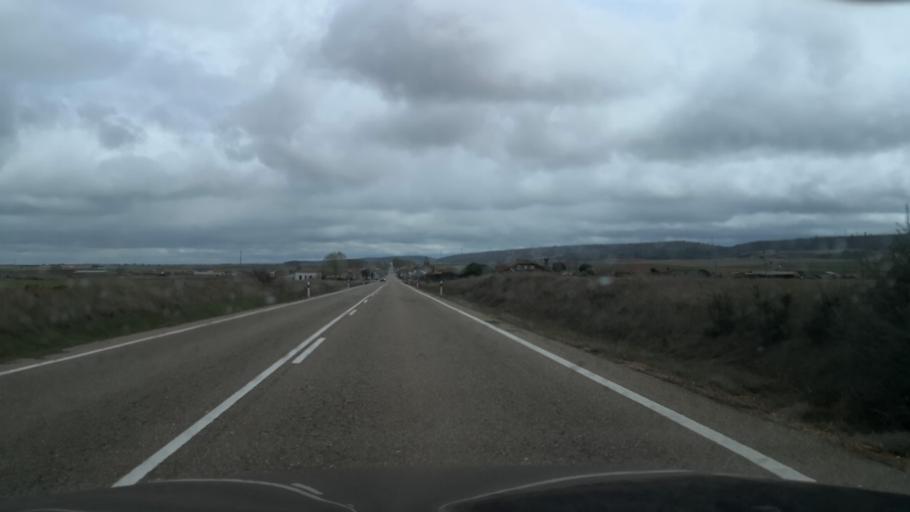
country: ES
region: Castille and Leon
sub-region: Provincia de Zamora
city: Pozuelo de Tabara
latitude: 41.7896
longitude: -5.9019
